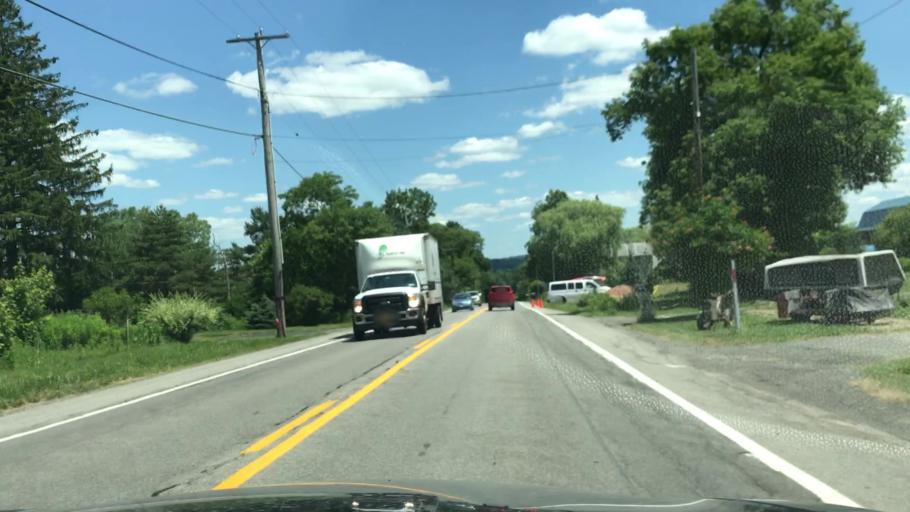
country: US
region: New York
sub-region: Erie County
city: East Aurora
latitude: 42.7676
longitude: -78.5610
